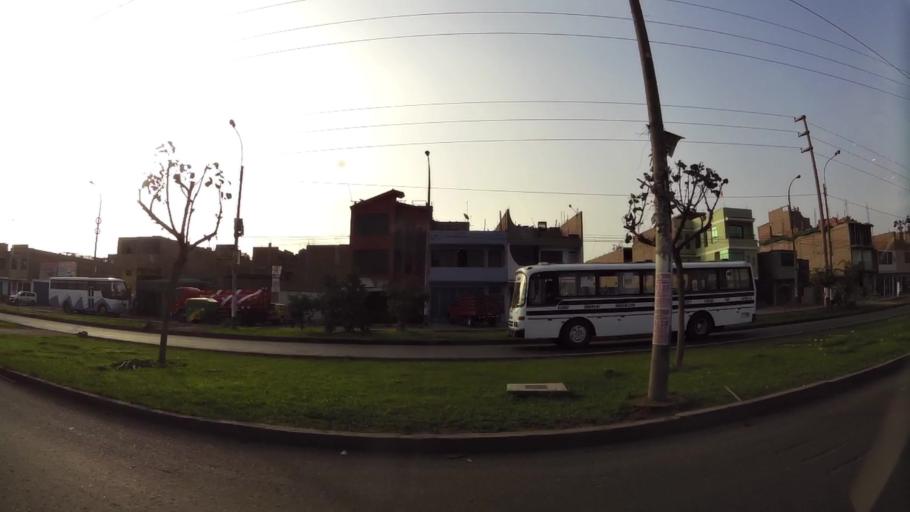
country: PE
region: Lima
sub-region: Lima
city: Independencia
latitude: -11.9496
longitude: -77.0833
